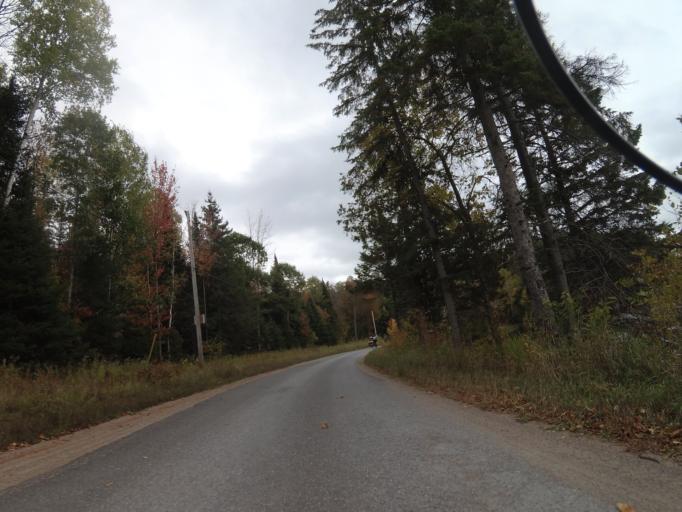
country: CA
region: Ontario
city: Renfrew
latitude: 45.2524
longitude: -77.1897
